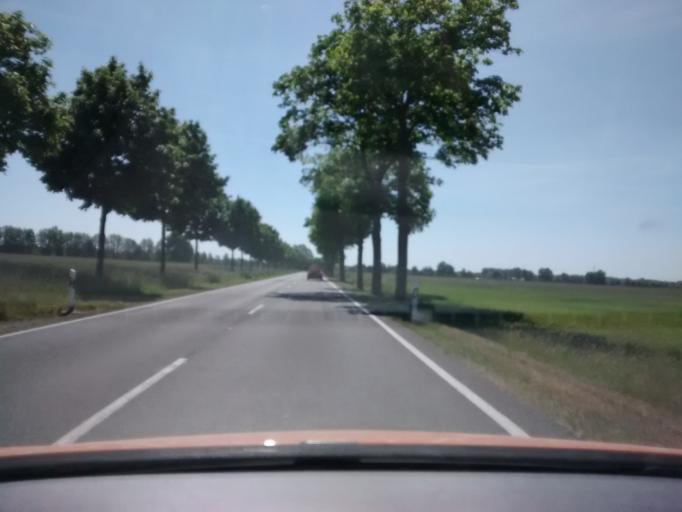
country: DE
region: Brandenburg
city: Storkow
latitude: 52.2929
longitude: 13.9046
